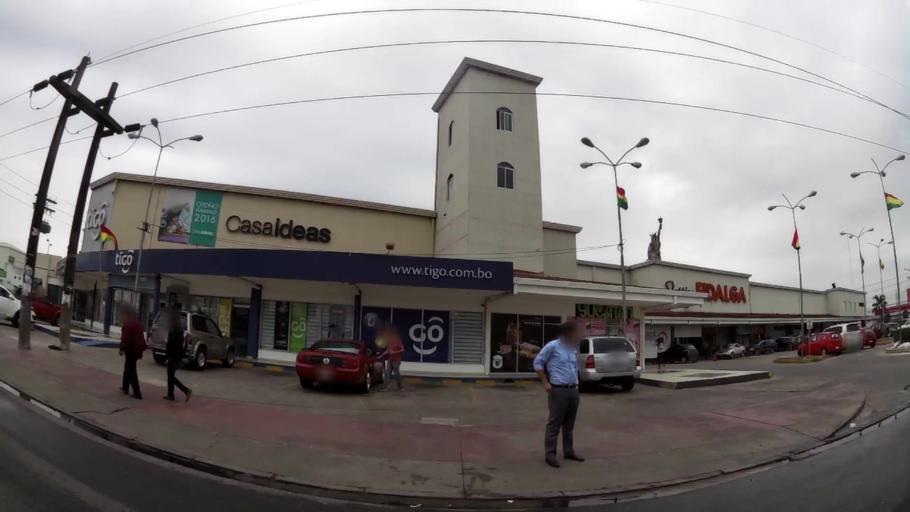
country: BO
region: Santa Cruz
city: Santa Cruz de la Sierra
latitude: -17.7584
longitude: -63.1785
